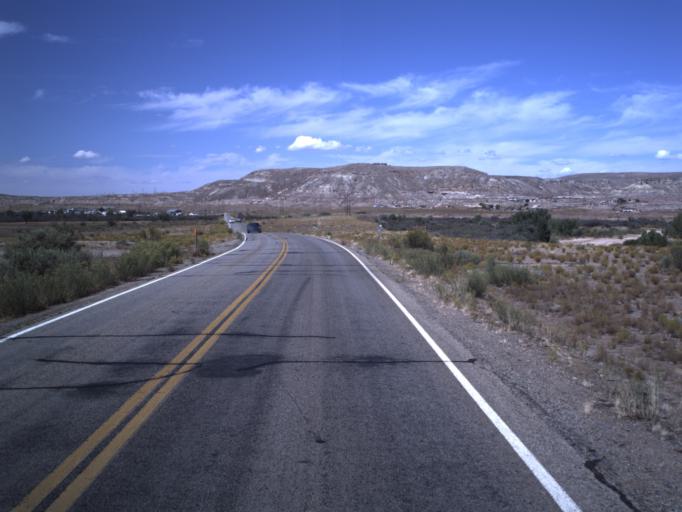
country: US
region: Utah
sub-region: San Juan County
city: Blanding
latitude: 37.2674
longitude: -109.3160
